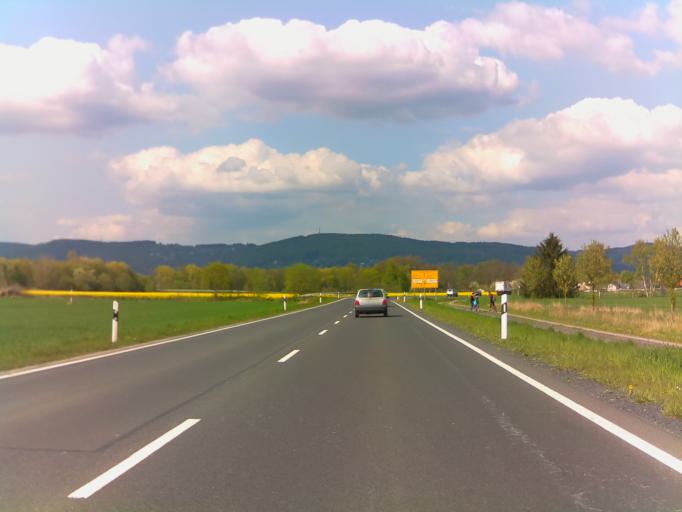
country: DE
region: Bavaria
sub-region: Upper Franconia
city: Ebersdorf
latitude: 50.3226
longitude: 11.1611
